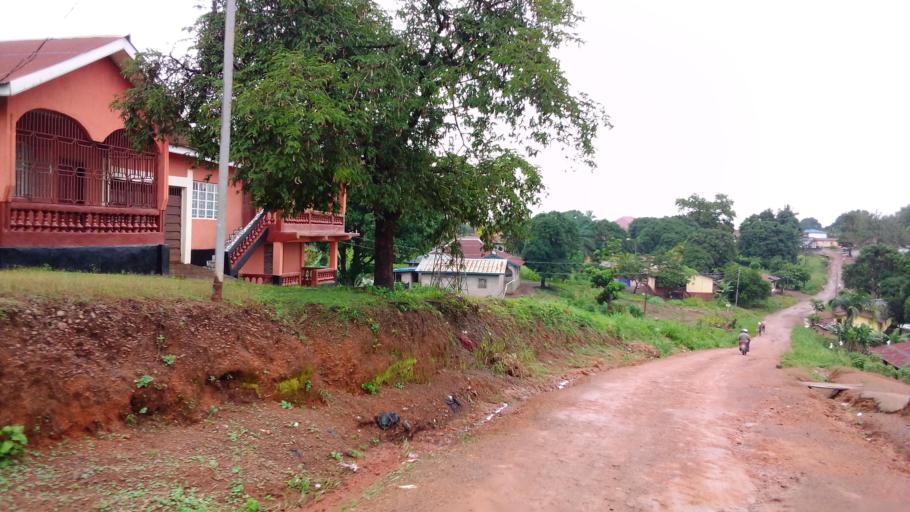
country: SL
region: Eastern Province
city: Kenema
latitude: 7.8972
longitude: -11.1814
